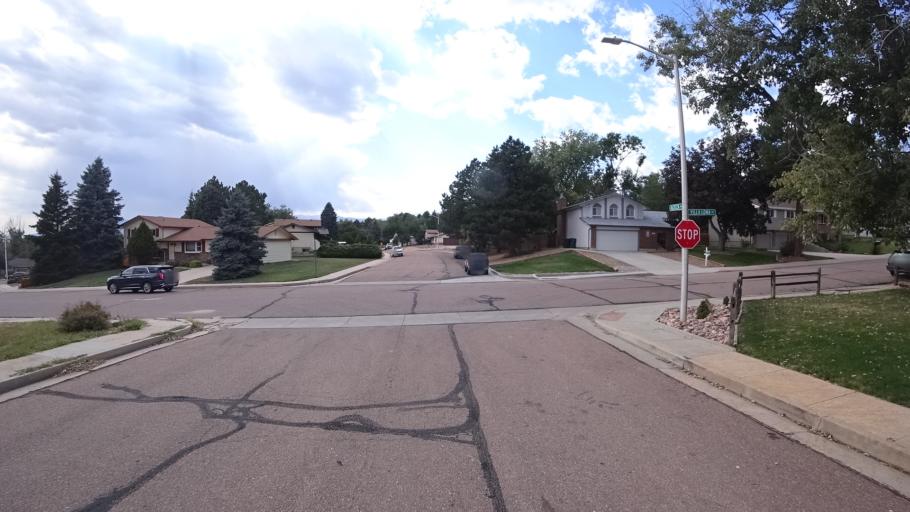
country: US
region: Colorado
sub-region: El Paso County
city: Cimarron Hills
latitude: 38.8696
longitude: -104.7310
